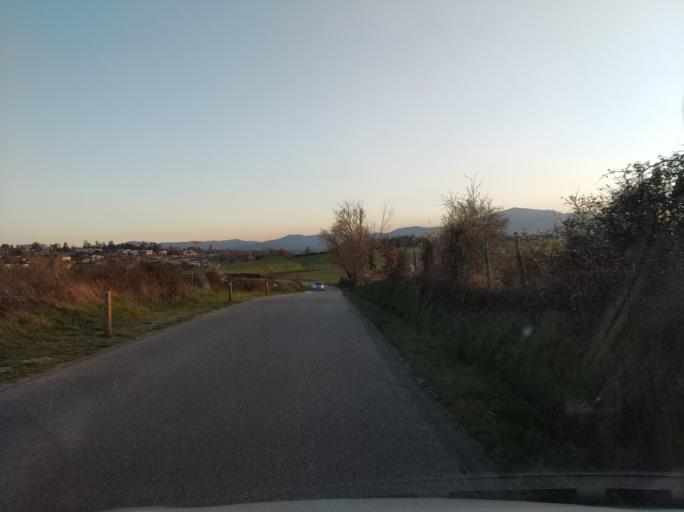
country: FR
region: Rhone-Alpes
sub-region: Departement de l'Ardeche
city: Boulieu-les-Annonay
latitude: 45.2657
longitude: 4.6863
